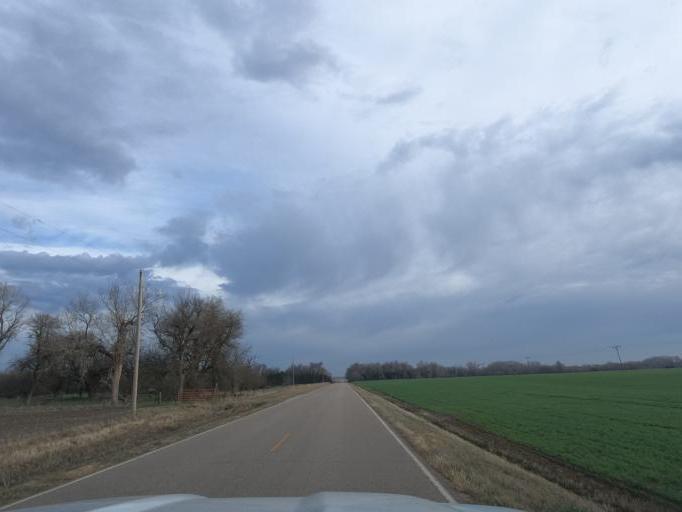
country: US
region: Kansas
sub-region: Reno County
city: South Hutchinson
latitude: 37.9275
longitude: -98.0872
